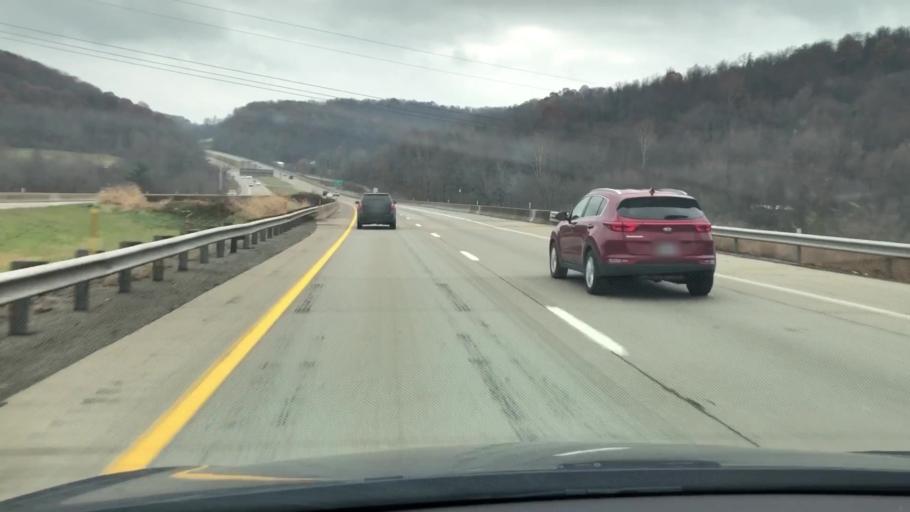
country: US
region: Pennsylvania
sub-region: Westmoreland County
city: New Stanton
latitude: 40.2131
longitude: -79.5908
